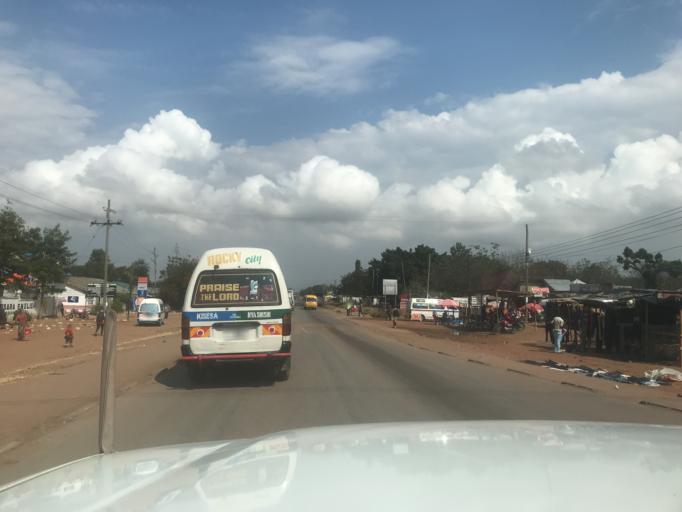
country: TZ
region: Mwanza
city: Usagara
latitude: -2.5554
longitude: 33.0465
